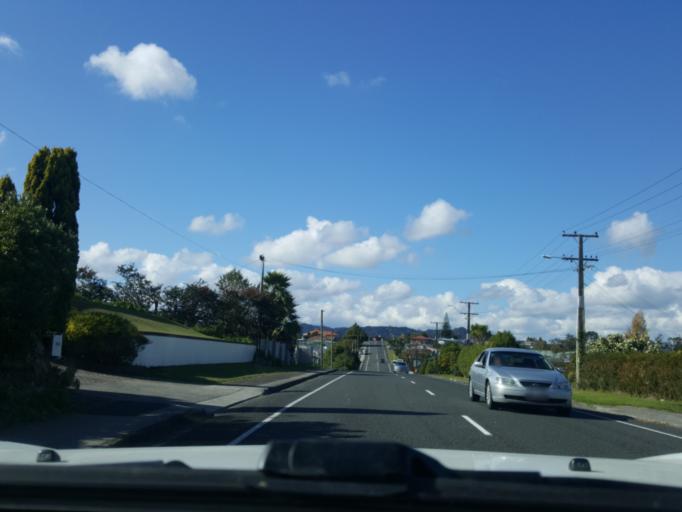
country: NZ
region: Waikato
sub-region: Waikato District
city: Ngaruawahia
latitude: -37.5481
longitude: 175.1635
